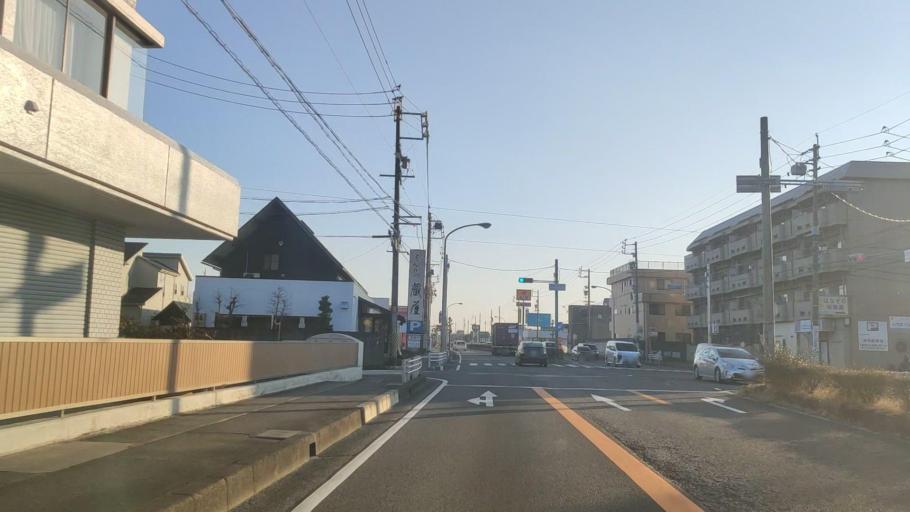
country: JP
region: Gifu
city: Gifu-shi
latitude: 35.4456
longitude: 136.7398
